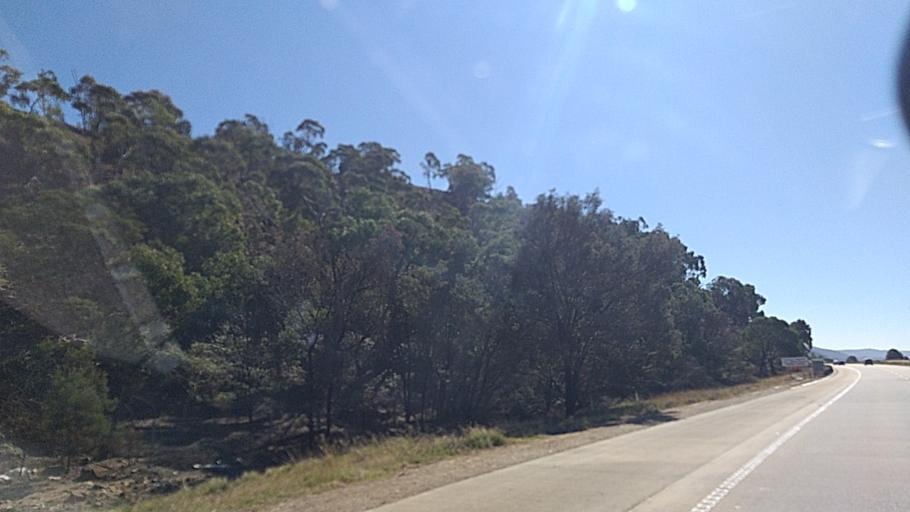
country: AU
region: New South Wales
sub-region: Yass Valley
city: Gundaroo
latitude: -35.0871
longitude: 149.3745
